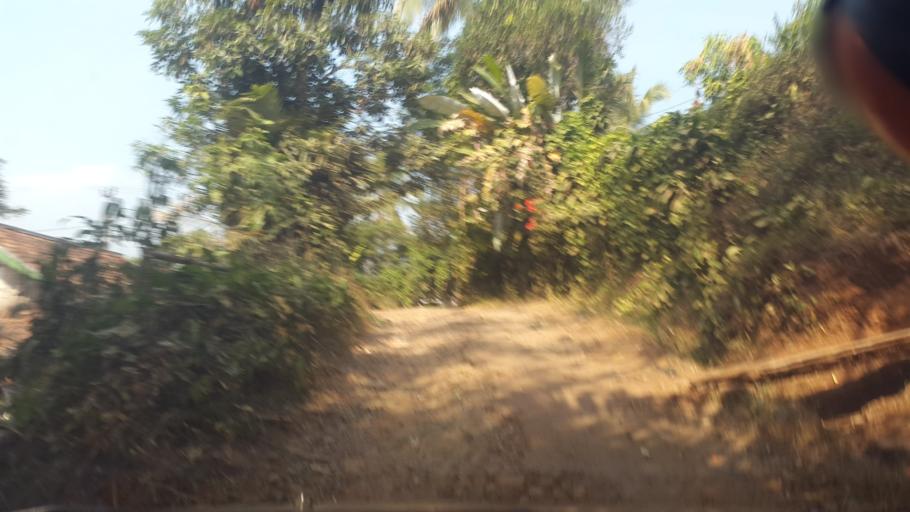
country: ID
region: West Java
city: Ciroyom
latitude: -7.1170
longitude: 106.8255
